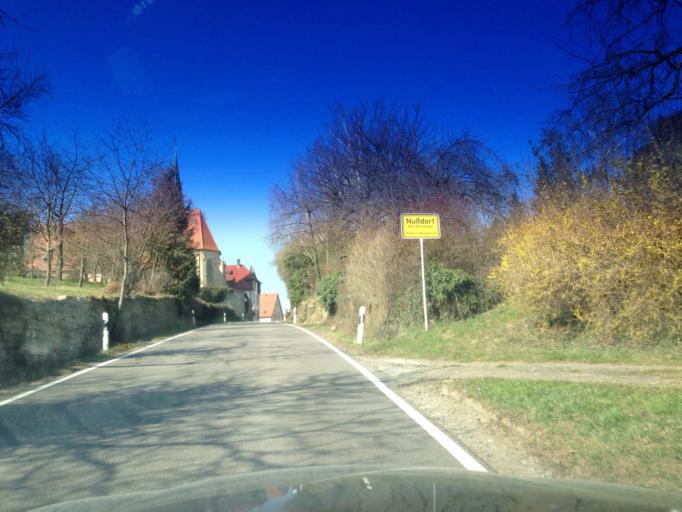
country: DE
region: Baden-Wuerttemberg
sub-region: Regierungsbezirk Stuttgart
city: Eberdingen
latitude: 48.8912
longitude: 8.9399
